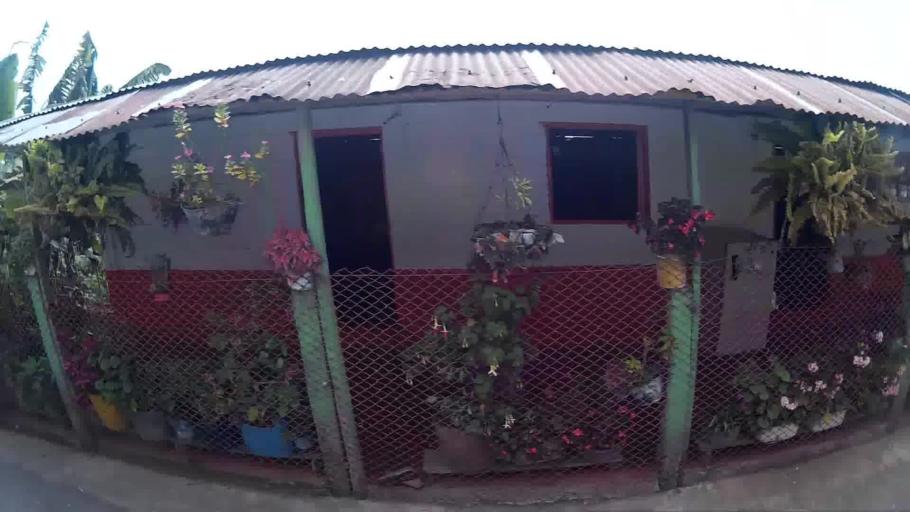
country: CO
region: Caldas
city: Belalcazar
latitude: 4.9584
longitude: -75.8276
